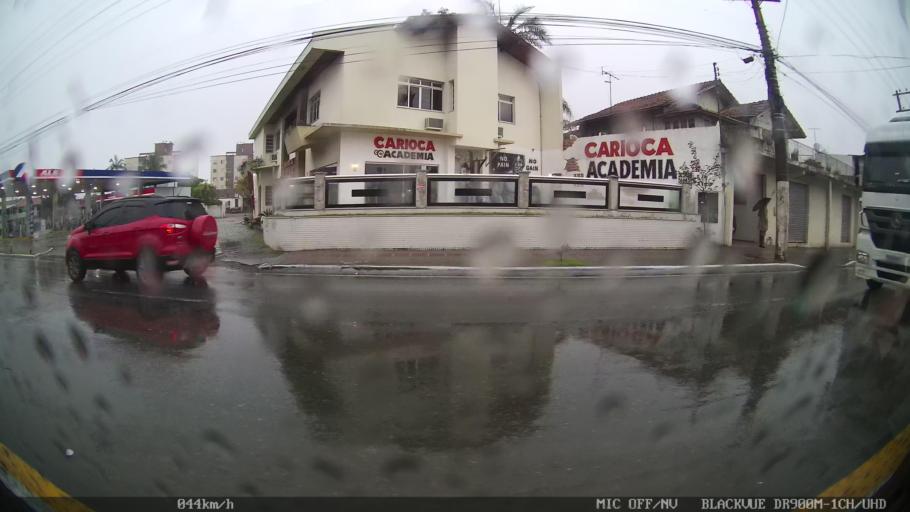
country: BR
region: Santa Catarina
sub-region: Itajai
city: Itajai
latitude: -26.8843
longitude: -48.6925
